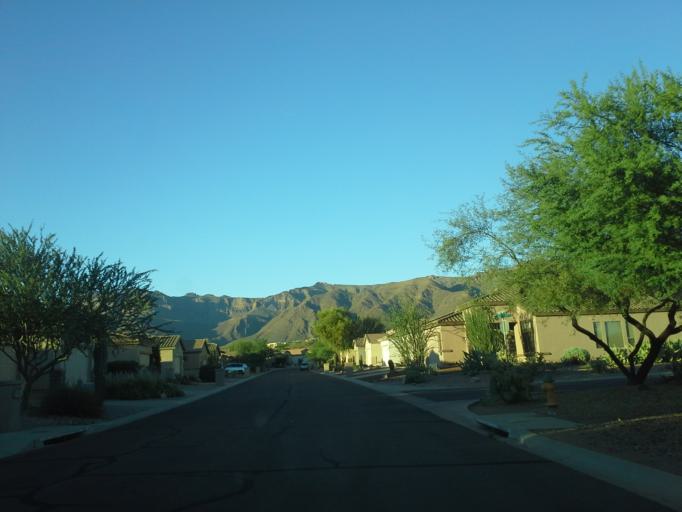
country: US
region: Arizona
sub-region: Pinal County
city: Apache Junction
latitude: 33.3745
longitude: -111.4386
